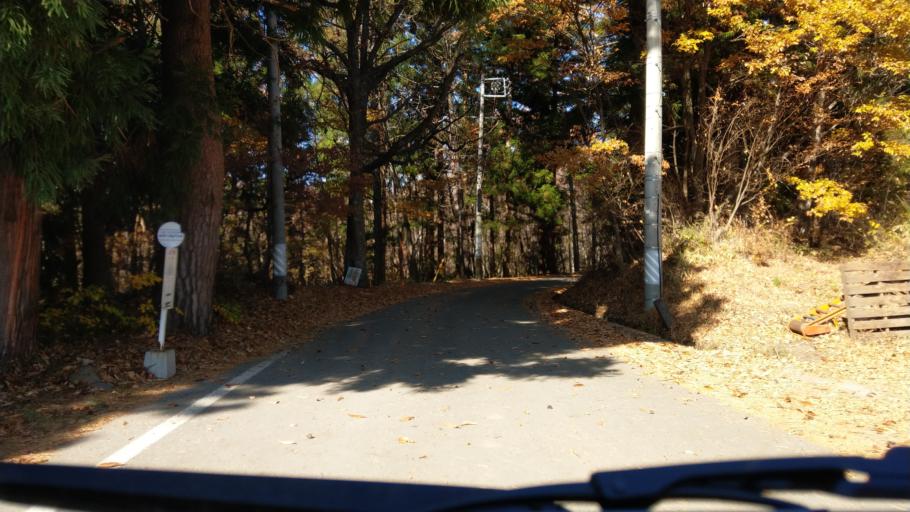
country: JP
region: Nagano
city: Komoro
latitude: 36.3552
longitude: 138.4554
